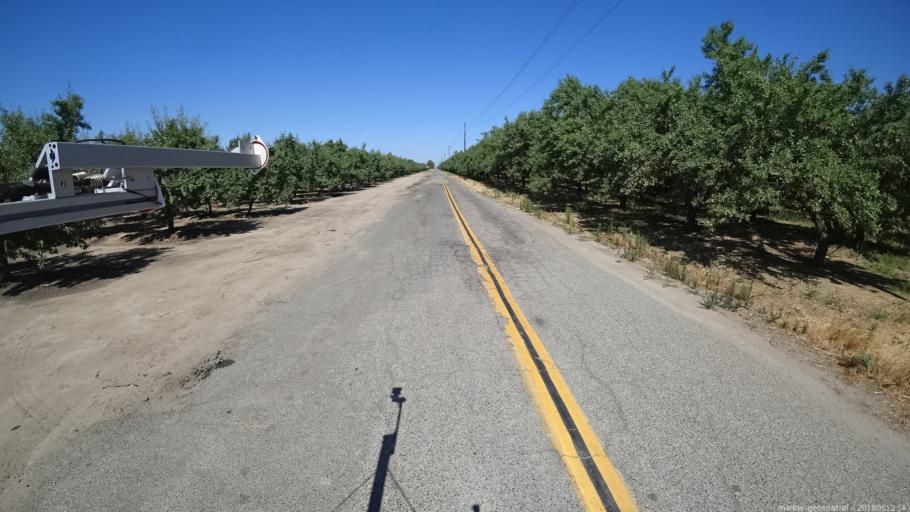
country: US
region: California
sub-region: Madera County
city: Chowchilla
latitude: 37.0325
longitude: -120.3835
